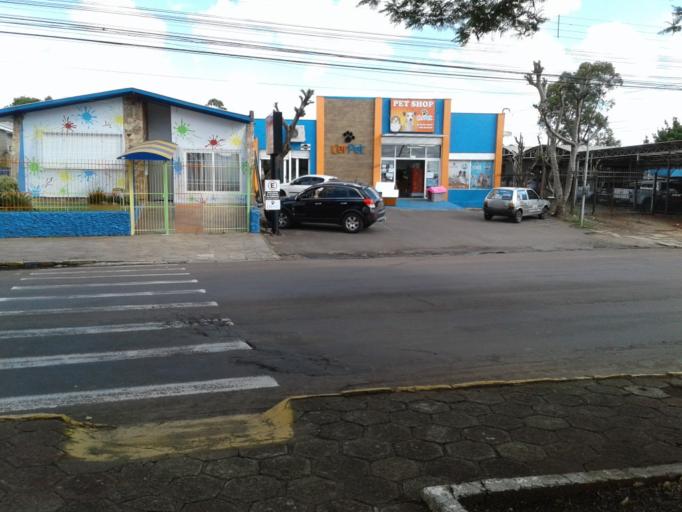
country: BR
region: Rio Grande do Sul
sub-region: Passo Fundo
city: Passo Fundo
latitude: -28.2692
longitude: -52.4255
